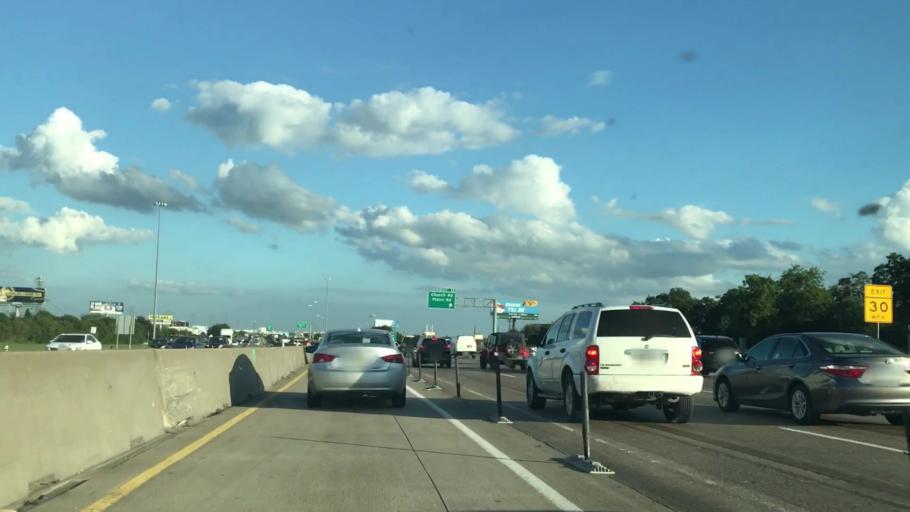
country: US
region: Texas
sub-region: Dallas County
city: Richardson
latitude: 32.8885
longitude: -96.7056
